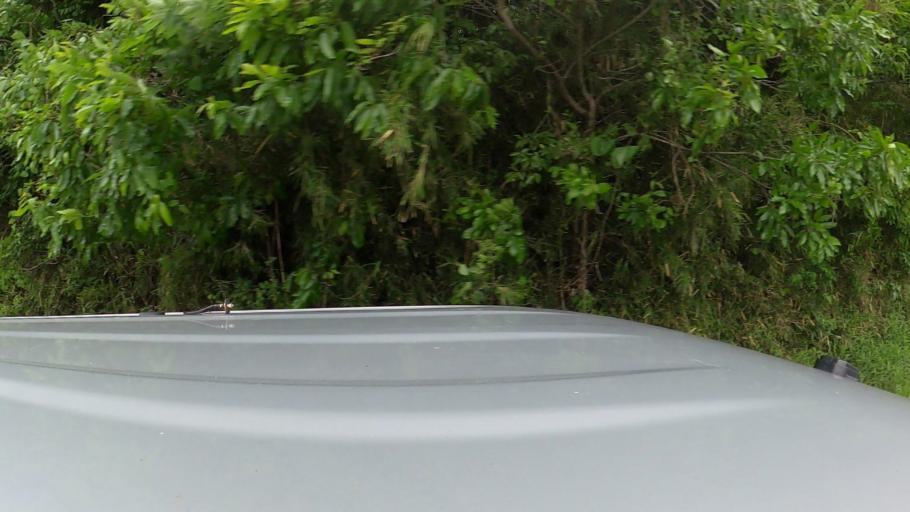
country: JP
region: Ibaraki
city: Edosaki
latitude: 35.9947
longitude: 140.2622
